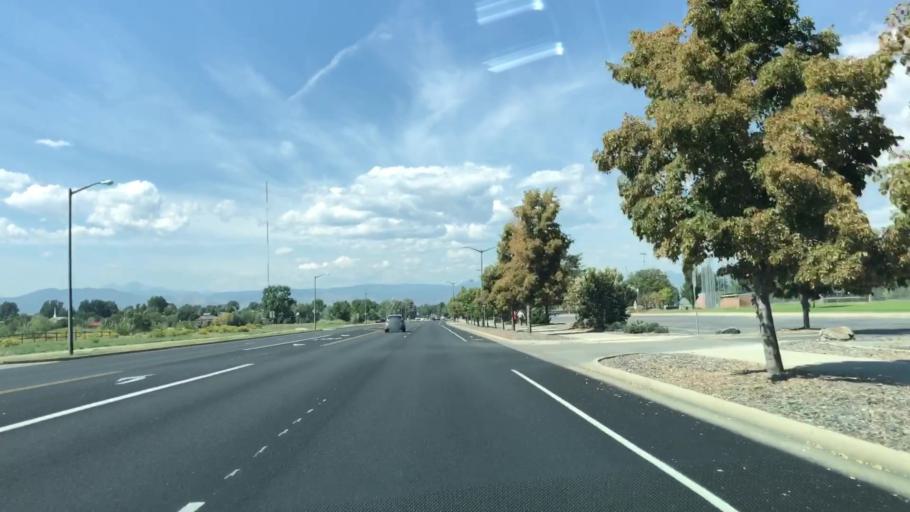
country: US
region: Colorado
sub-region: Larimer County
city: Loveland
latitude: 40.3928
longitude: -105.0902
